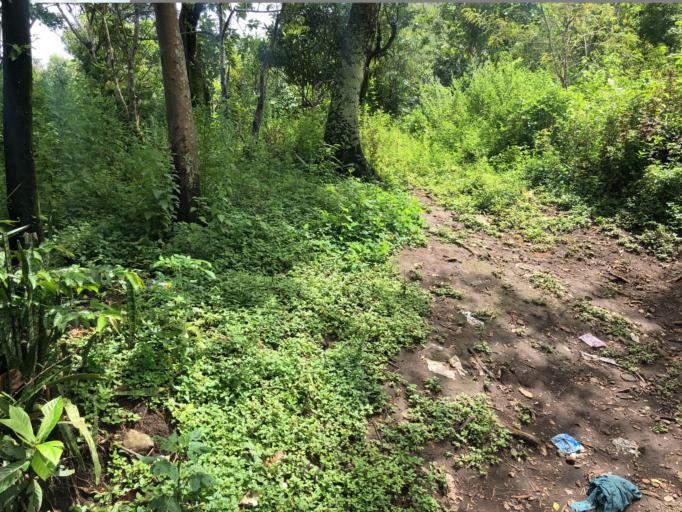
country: GT
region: Escuintla
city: San Vicente Pacaya
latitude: 14.3287
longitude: -90.6057
